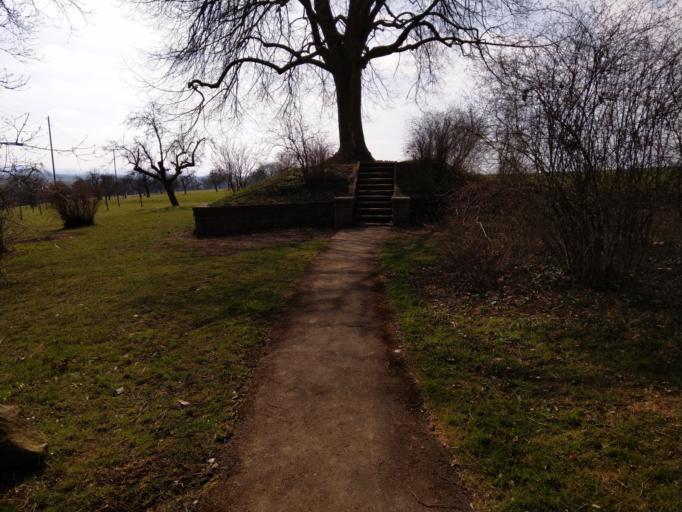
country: DE
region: Baden-Wuerttemberg
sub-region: Regierungsbezirk Stuttgart
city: Nurtingen
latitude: 48.6292
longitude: 9.3223
